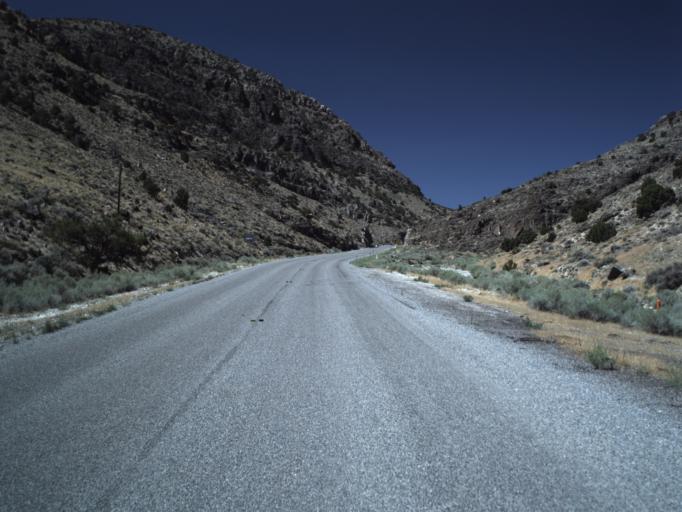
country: US
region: Utah
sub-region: Beaver County
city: Milford
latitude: 39.0855
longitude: -113.5800
